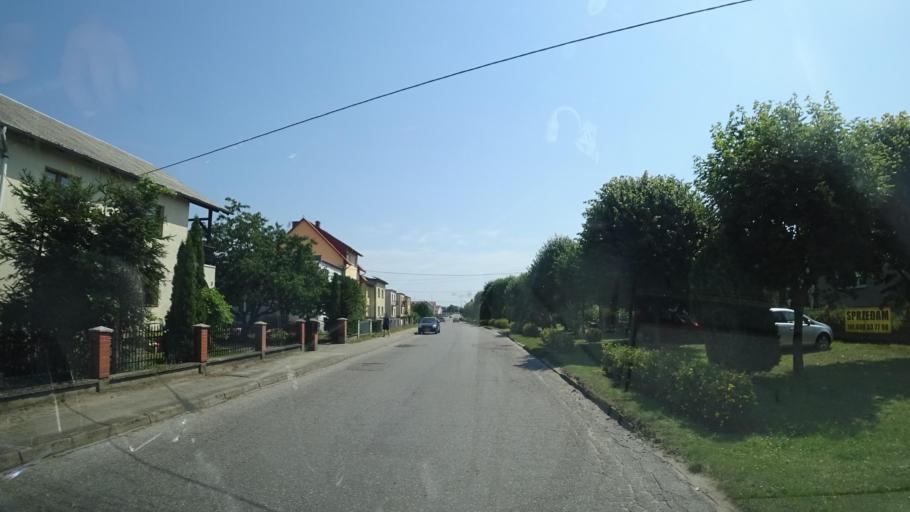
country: PL
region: Pomeranian Voivodeship
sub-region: Powiat chojnicki
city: Brusy
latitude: 53.8845
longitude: 17.7086
